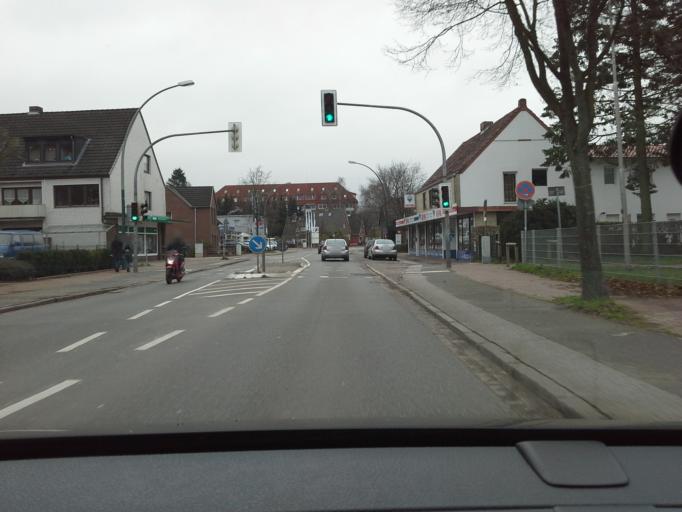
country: DE
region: Schleswig-Holstein
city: Pinneberg
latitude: 53.6680
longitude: 9.7937
